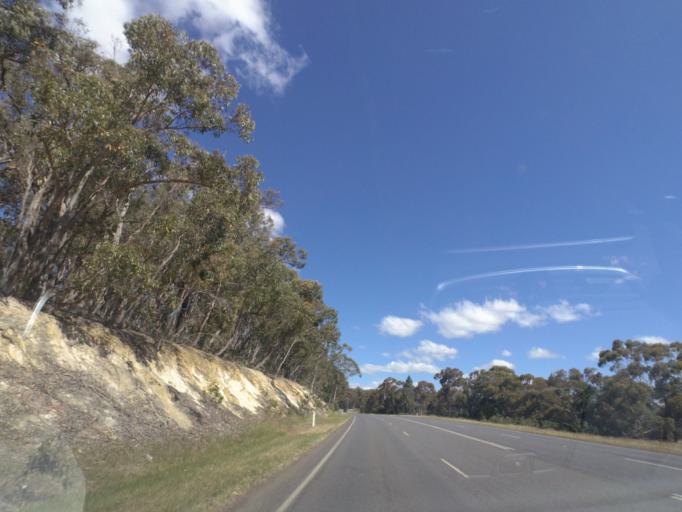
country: AU
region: Victoria
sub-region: Hume
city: Sunbury
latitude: -37.4388
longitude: 144.5649
